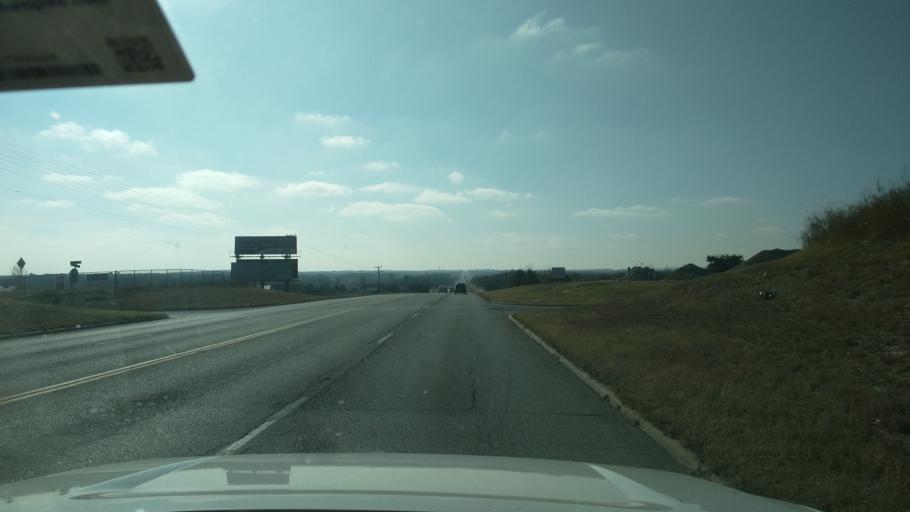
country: US
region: Oklahoma
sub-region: Washington County
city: Bartlesville
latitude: 36.6854
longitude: -95.9352
